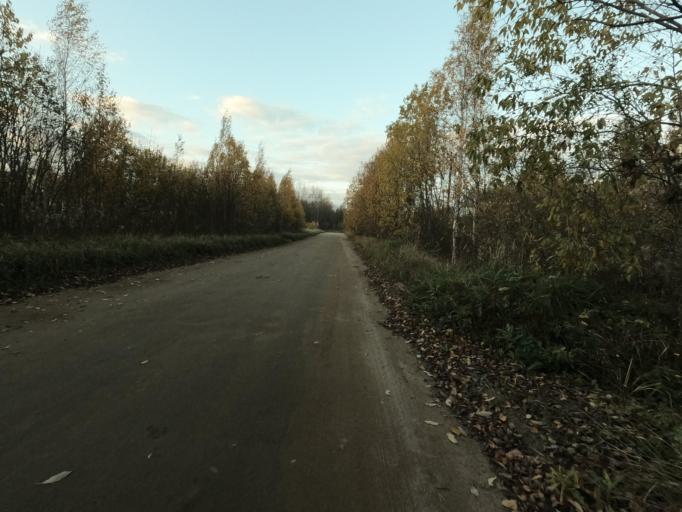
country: RU
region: Leningrad
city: Mga
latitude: 59.8053
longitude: 31.2009
